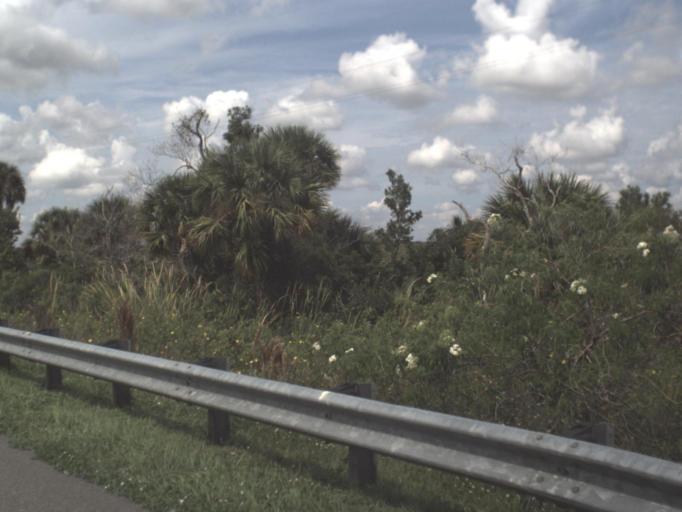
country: US
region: Florida
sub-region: Highlands County
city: Lake Placid
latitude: 27.2098
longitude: -81.1565
